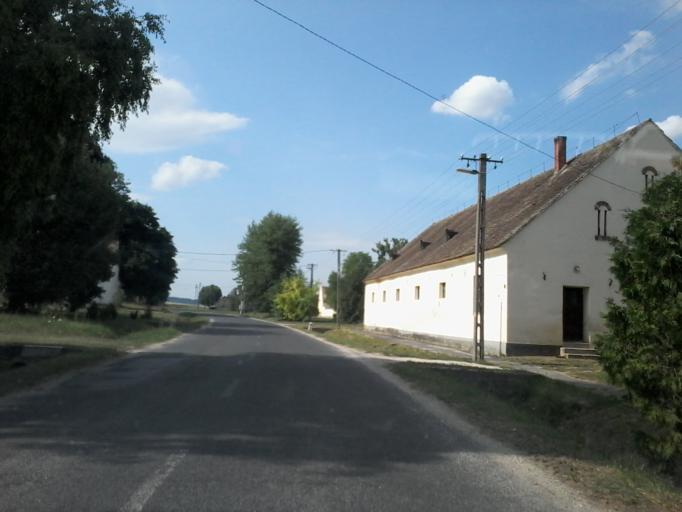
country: HU
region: Vas
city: Celldomolk
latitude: 47.2308
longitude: 17.0893
